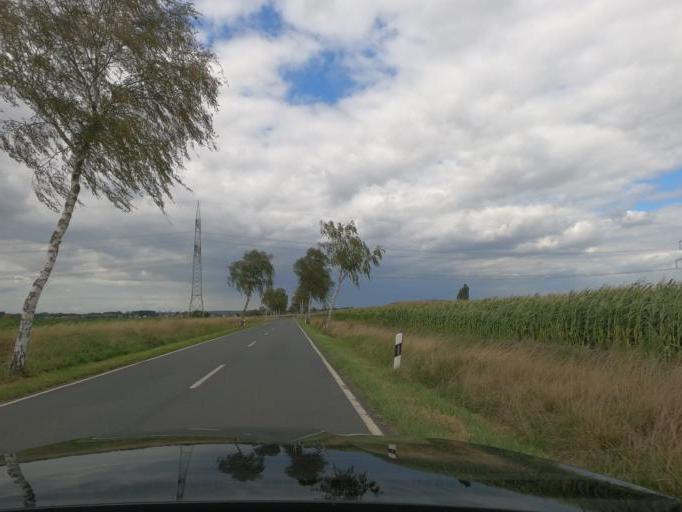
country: DE
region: Lower Saxony
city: Algermissen
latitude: 52.2814
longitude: 9.9501
